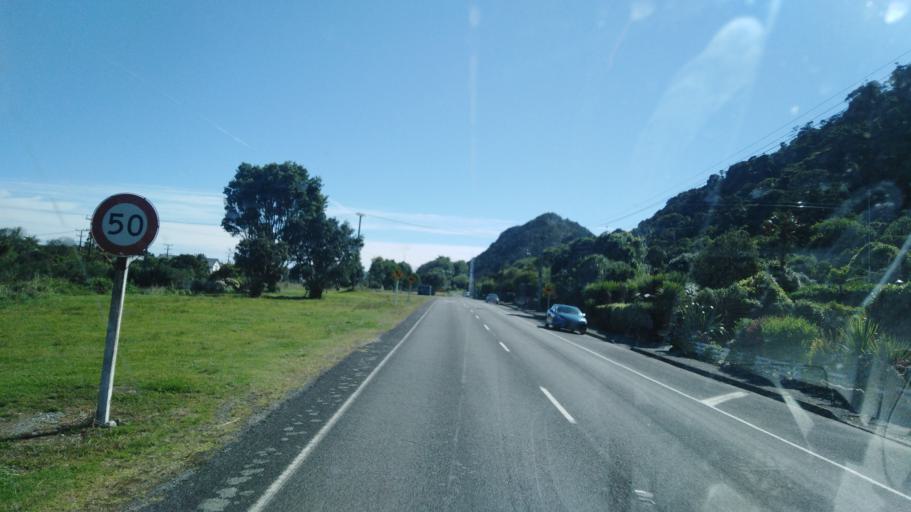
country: NZ
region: West Coast
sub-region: Buller District
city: Westport
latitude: -41.6337
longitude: 171.8505
